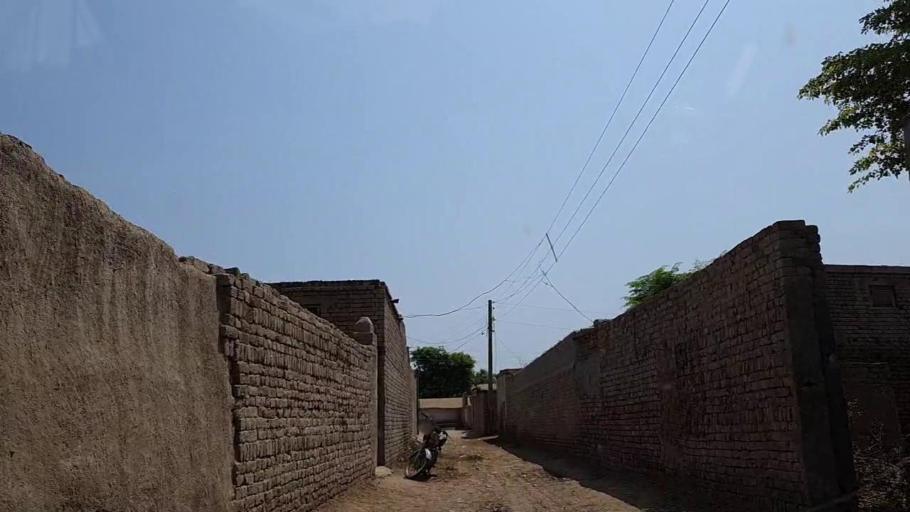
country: PK
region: Sindh
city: Adilpur
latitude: 27.9651
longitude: 69.3877
